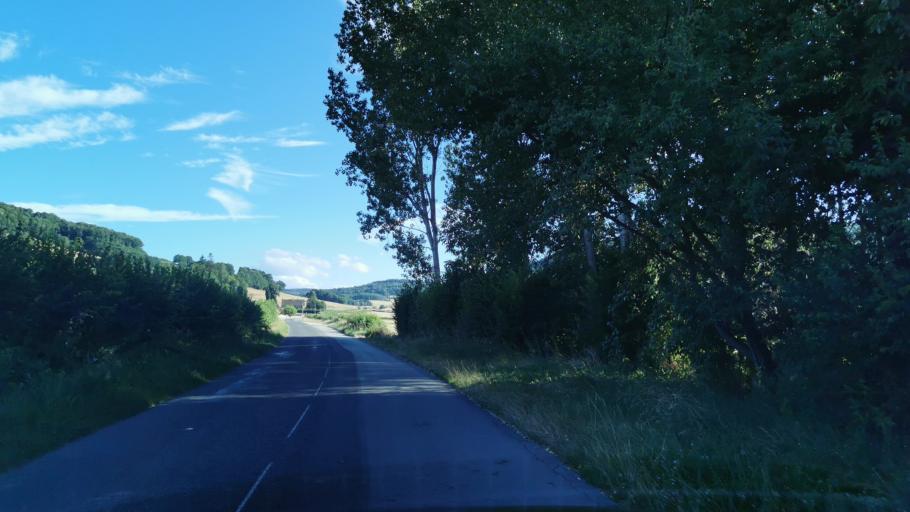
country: FR
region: Bourgogne
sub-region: Departement de Saone-et-Loire
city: Marmagne
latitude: 46.8435
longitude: 4.3192
